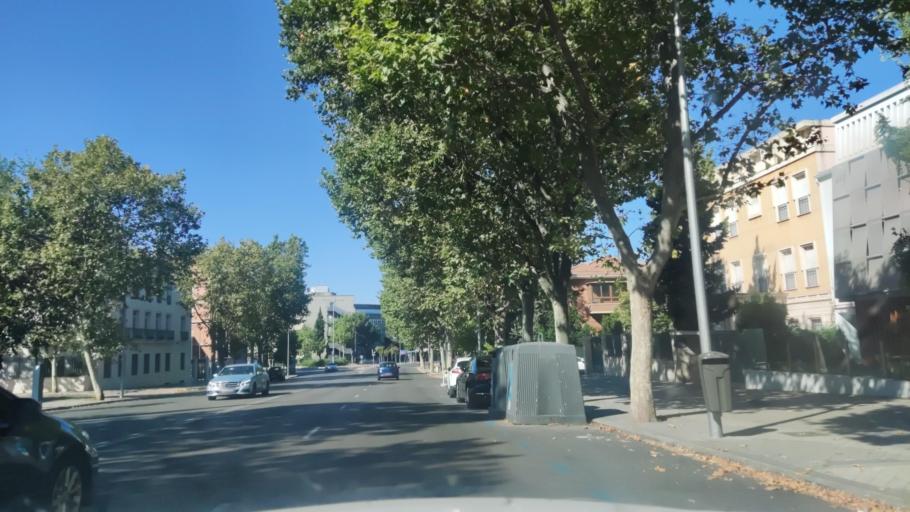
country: ES
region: Madrid
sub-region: Provincia de Madrid
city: Chamartin
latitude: 40.4470
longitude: -3.6813
